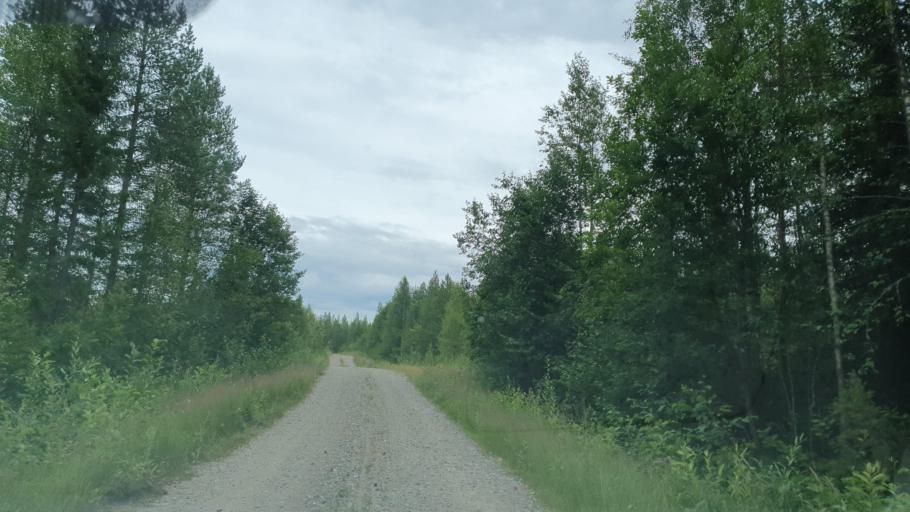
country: FI
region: Kainuu
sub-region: Kehys-Kainuu
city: Kuhmo
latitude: 64.2028
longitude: 29.4018
